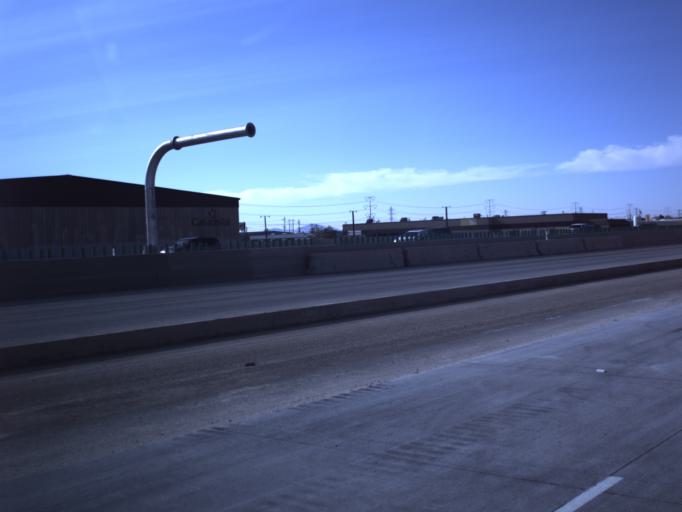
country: US
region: Utah
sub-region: Salt Lake County
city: Taylorsville
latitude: 40.7144
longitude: -111.9535
